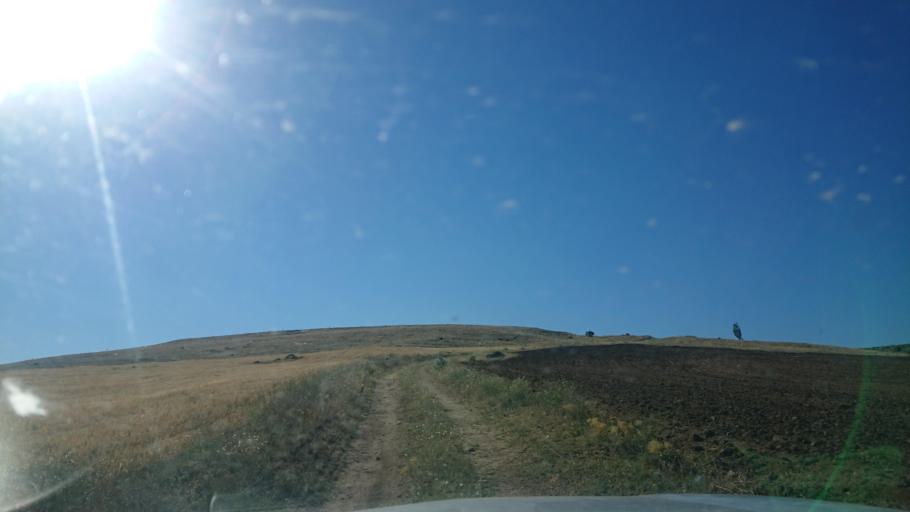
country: TR
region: Aksaray
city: Agacoren
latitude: 38.8389
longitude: 33.9353
